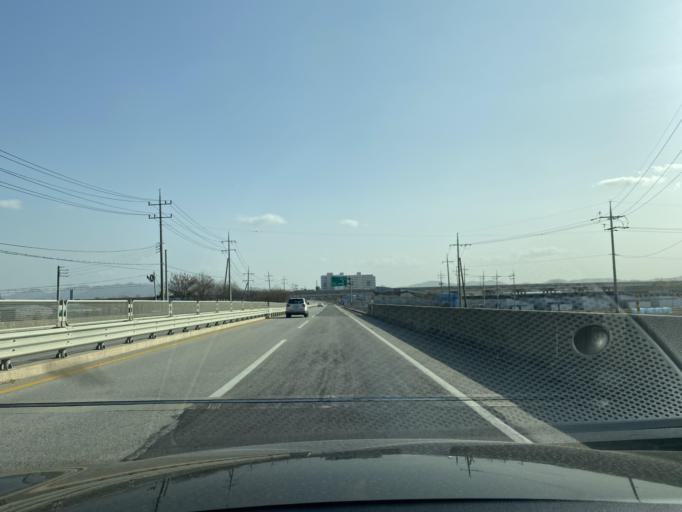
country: KR
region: Chungcheongnam-do
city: Yesan
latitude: 36.6865
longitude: 126.7675
